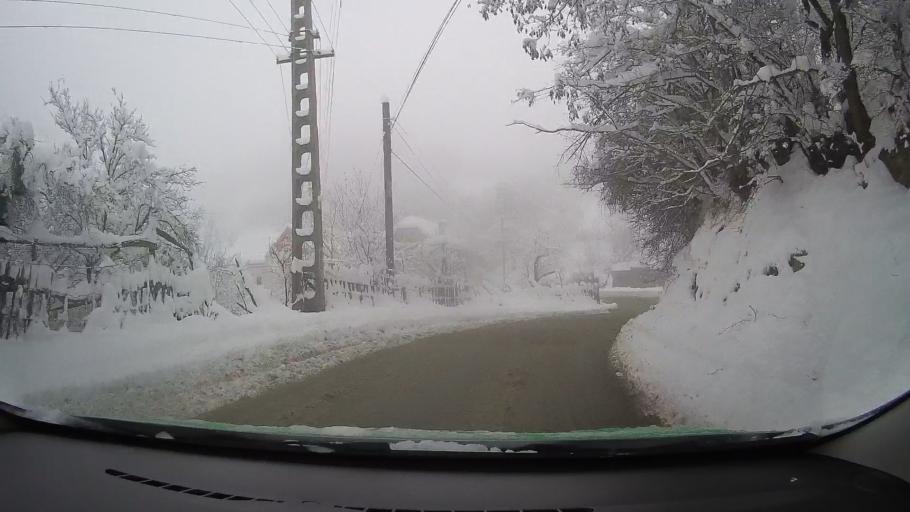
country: RO
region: Sibiu
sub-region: Comuna Poiana Sibiului
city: Poiana Sibiului
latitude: 45.8046
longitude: 23.7741
